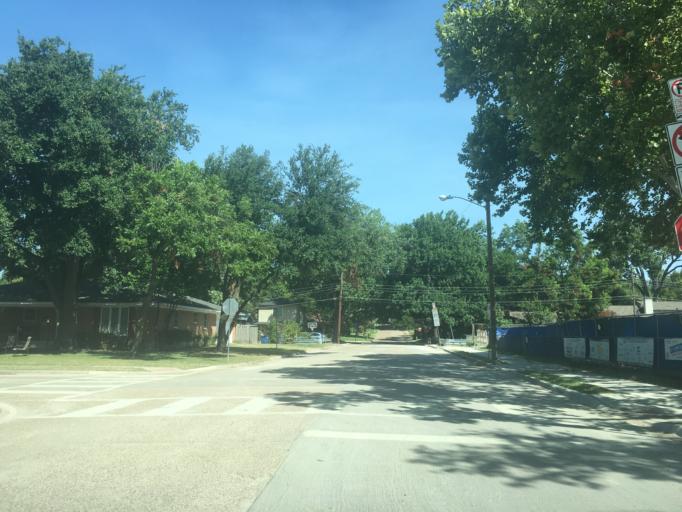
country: US
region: Texas
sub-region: Dallas County
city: Richardson
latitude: 32.8737
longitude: -96.7252
